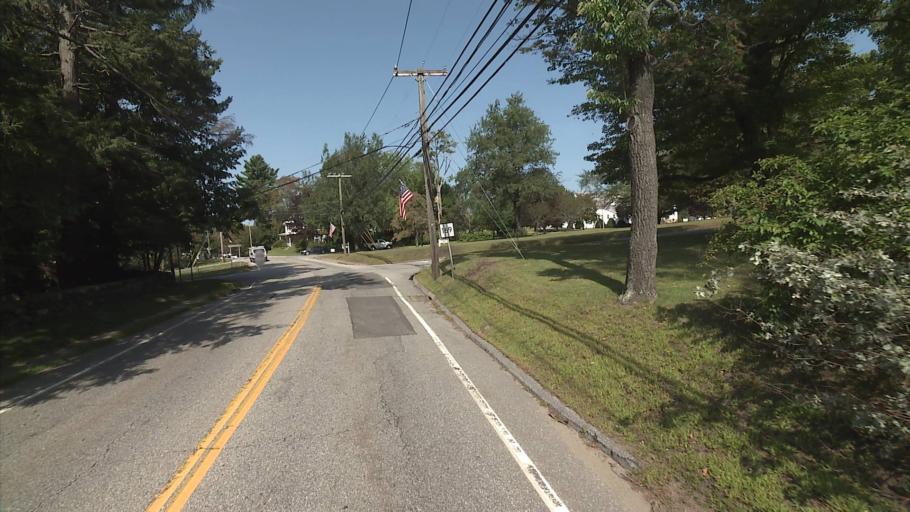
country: US
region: Connecticut
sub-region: Windham County
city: South Woodstock
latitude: 41.9505
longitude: -71.9771
